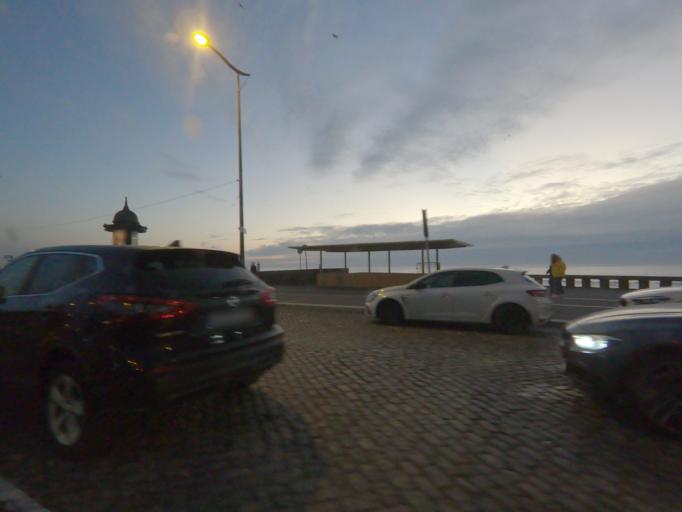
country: PT
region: Porto
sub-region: Matosinhos
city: Matosinhos
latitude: 41.1497
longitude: -8.6761
